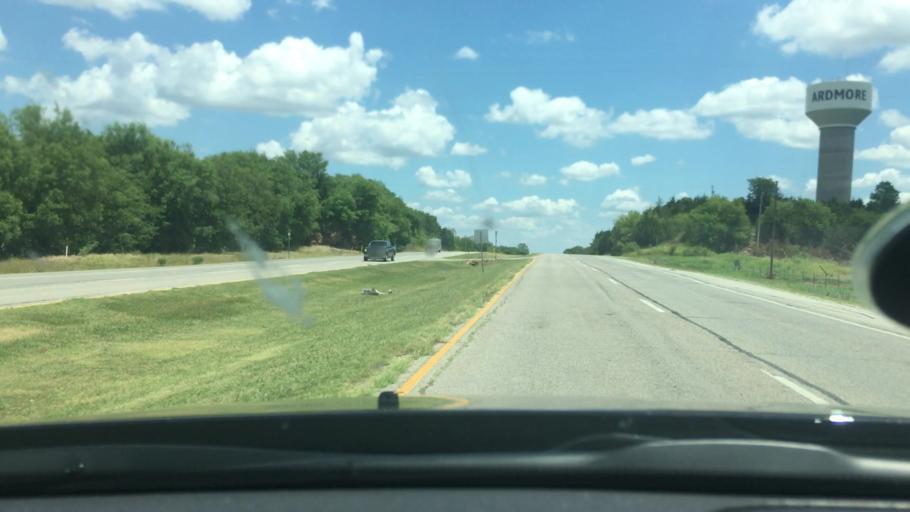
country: US
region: Oklahoma
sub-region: Carter County
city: Ardmore
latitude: 34.1730
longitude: -97.2010
